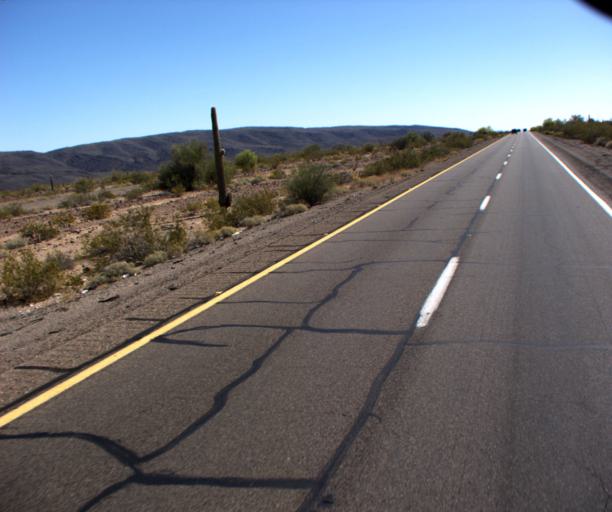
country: US
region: Arizona
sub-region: La Paz County
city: Quartzsite
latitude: 33.6542
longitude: -113.9503
